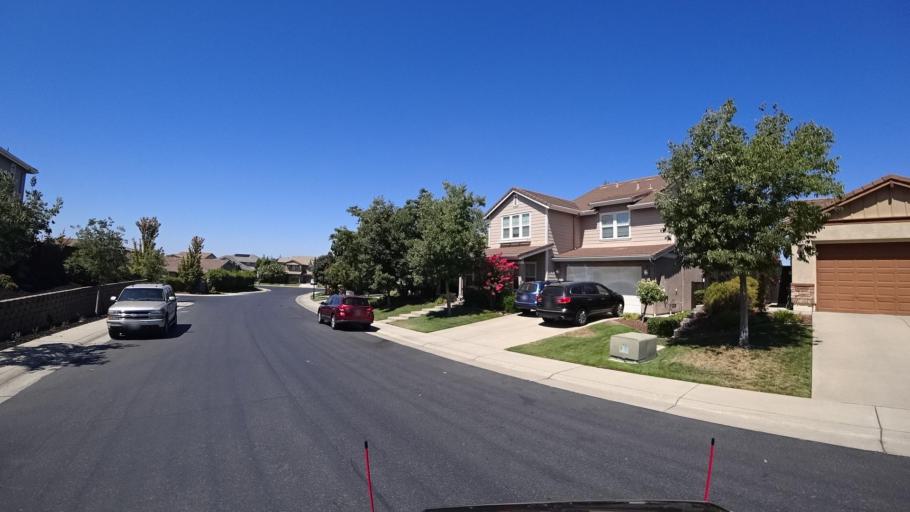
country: US
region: California
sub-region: Placer County
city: Rocklin
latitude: 38.8284
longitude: -121.2770
